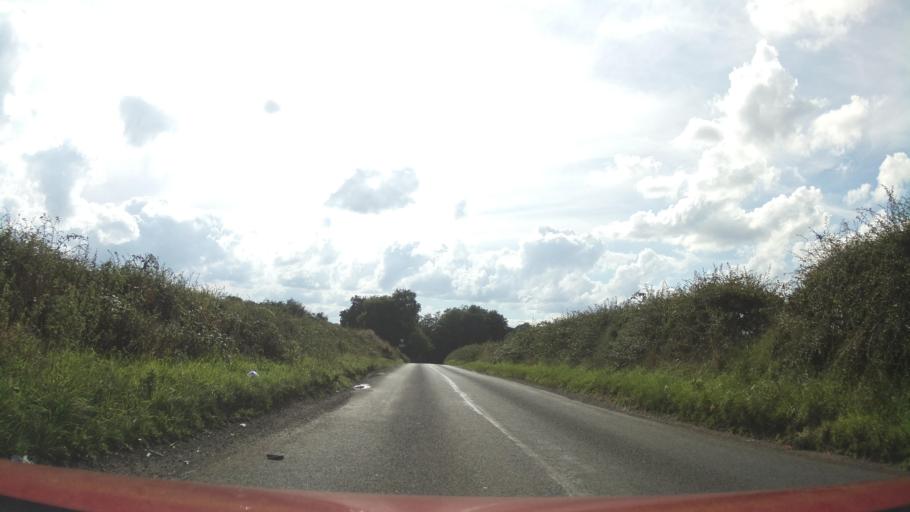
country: GB
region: Scotland
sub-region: Falkirk
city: Larbert
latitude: 56.0103
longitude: -3.8395
